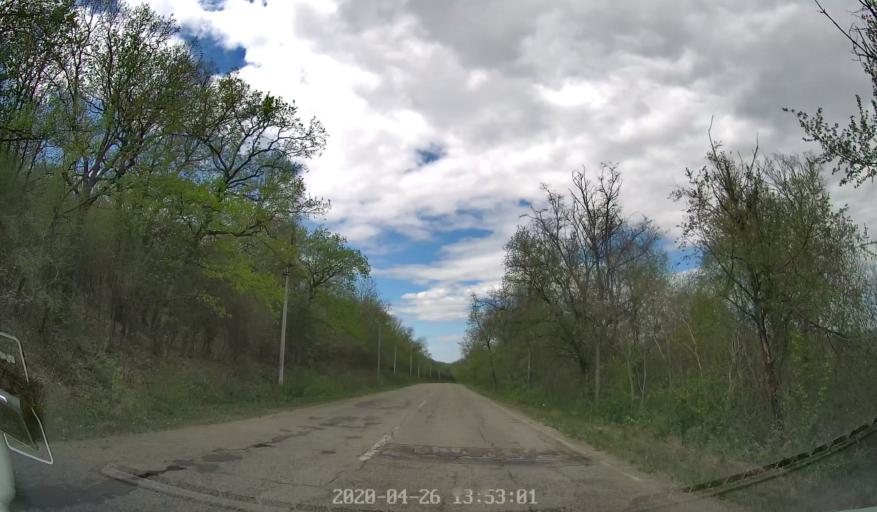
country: MD
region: Telenesti
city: Cocieri
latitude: 47.2760
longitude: 29.1134
